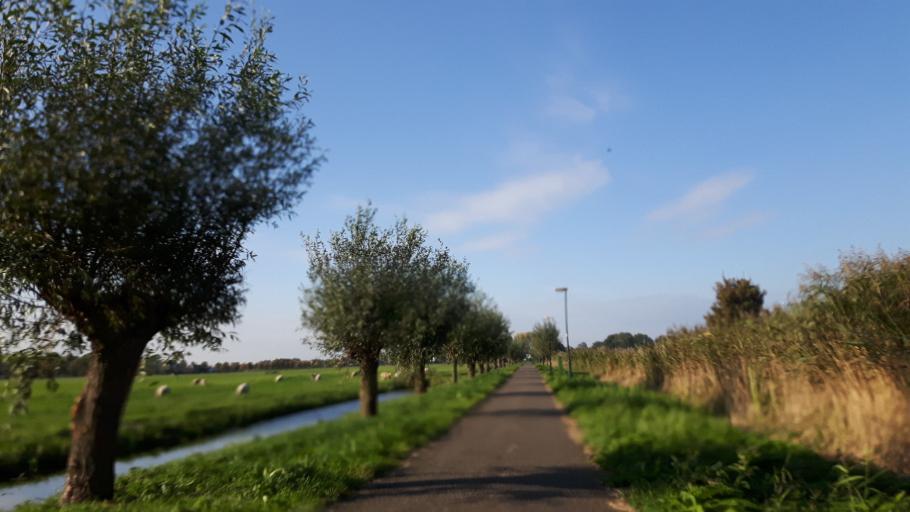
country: NL
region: Utrecht
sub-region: Gemeente Oudewater
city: Oudewater
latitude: 52.0110
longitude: 4.8842
